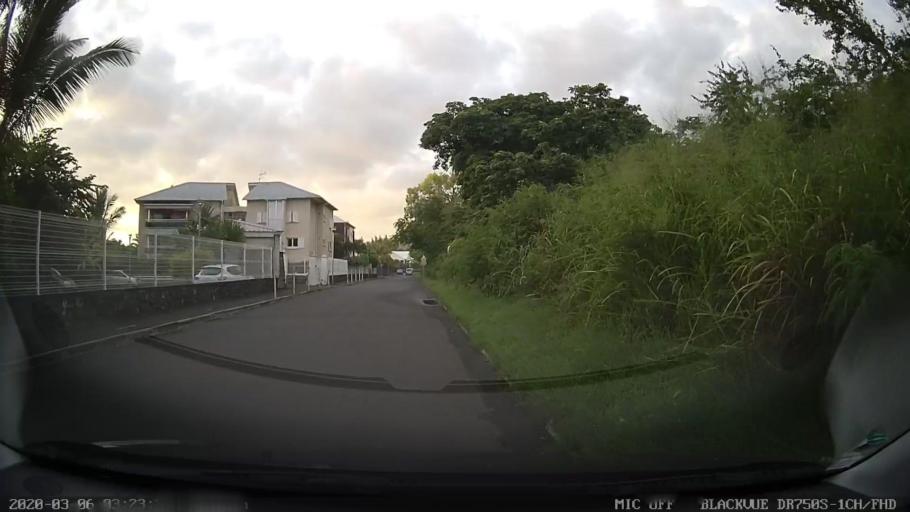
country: RE
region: Reunion
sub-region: Reunion
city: Les Avirons
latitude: -21.2686
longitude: 55.3375
